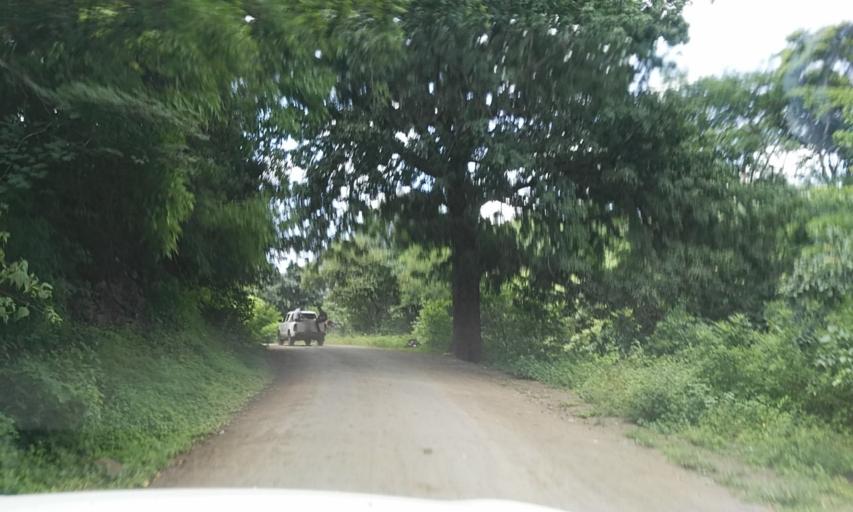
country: NI
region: Matagalpa
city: Terrabona
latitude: 12.7232
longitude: -85.9651
